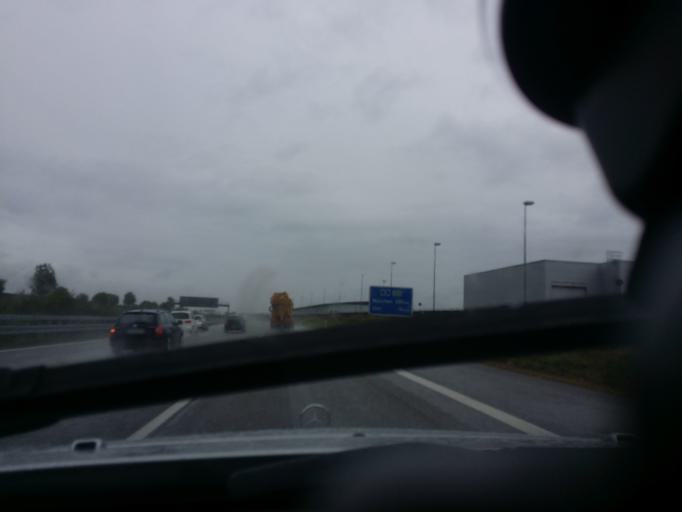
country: DE
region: Baden-Wuerttemberg
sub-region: Regierungsbezirk Stuttgart
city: Leinfelden-Echterdingen
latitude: 48.6930
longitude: 9.2043
